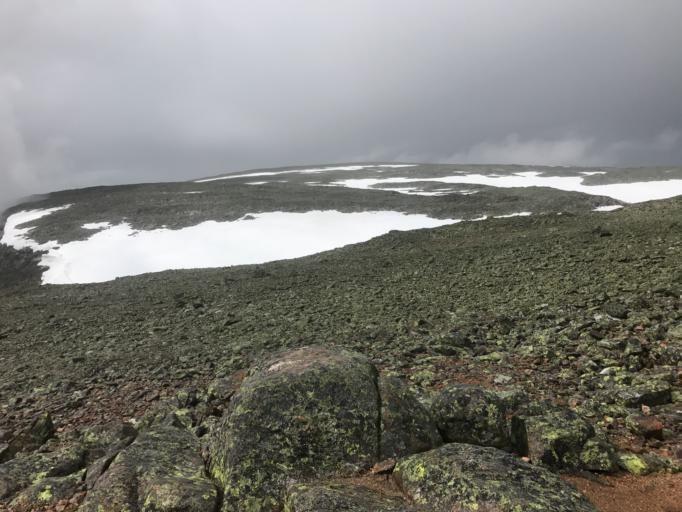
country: NO
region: Buskerud
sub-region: Hol
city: Geilo
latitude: 60.5588
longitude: 8.0542
